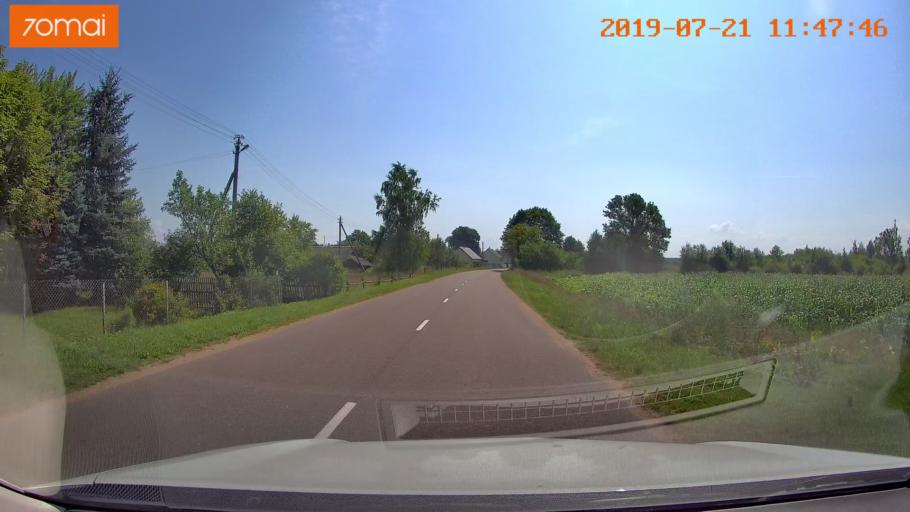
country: BY
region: Grodnenskaya
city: Lyubcha
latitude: 53.9013
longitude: 26.0527
